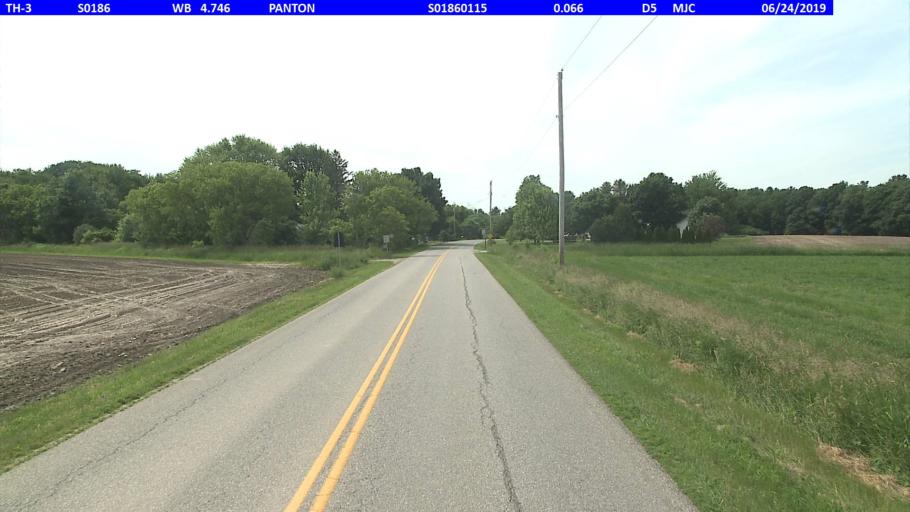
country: US
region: Vermont
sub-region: Addison County
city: Vergennes
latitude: 44.1621
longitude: -73.2925
